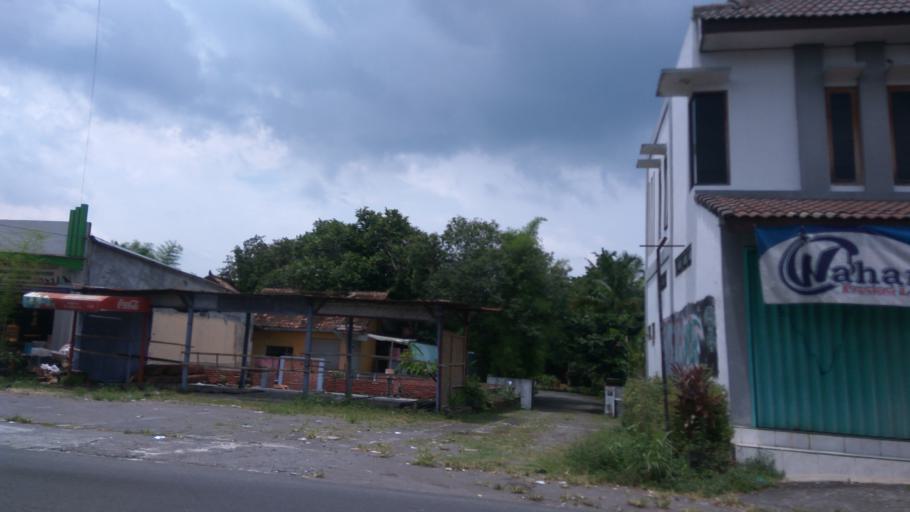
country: ID
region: Daerah Istimewa Yogyakarta
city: Melati
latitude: -7.7246
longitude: 110.4011
